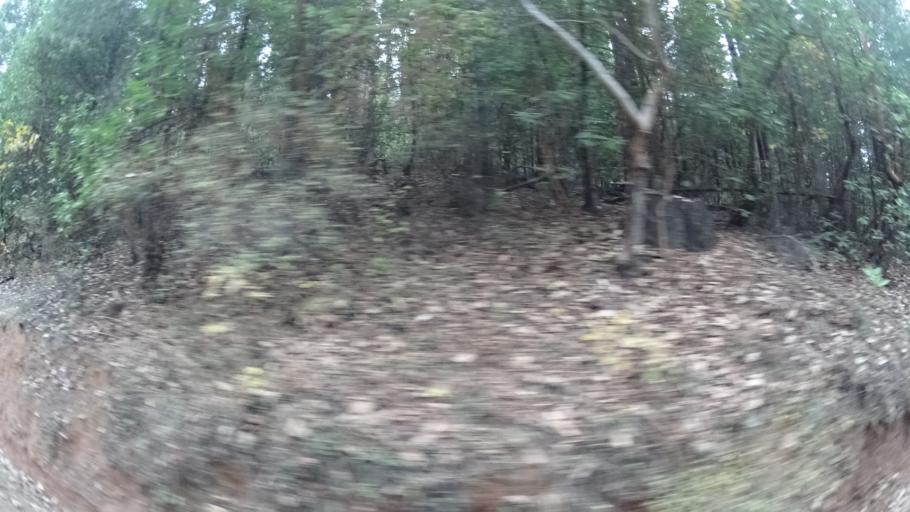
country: US
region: California
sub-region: Siskiyou County
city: Happy Camp
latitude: 41.7827
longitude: -123.3306
